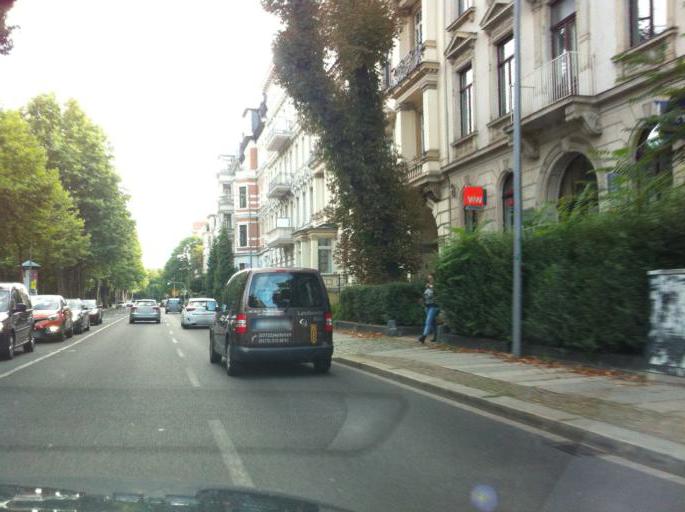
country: DE
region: Saxony
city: Leipzig
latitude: 51.3315
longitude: 12.3714
